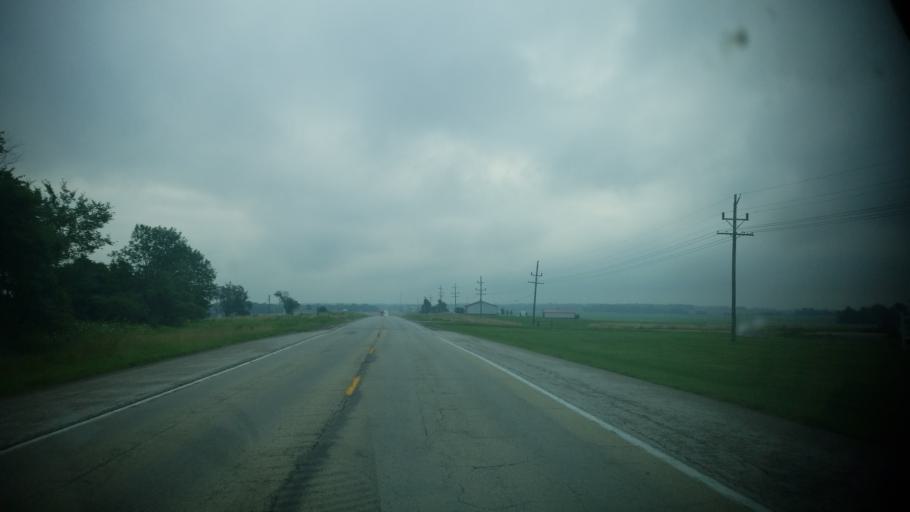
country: US
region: Illinois
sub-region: Clay County
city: Flora
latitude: 38.6774
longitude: -88.3928
